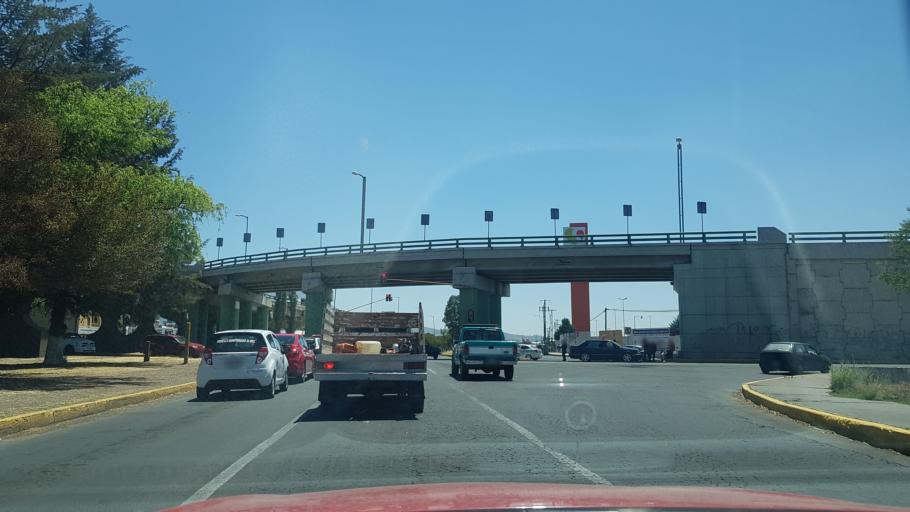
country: MX
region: Mexico
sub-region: Atlacomulco
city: Santa Cruz Bombatevi
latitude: 19.7933
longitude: -99.8880
